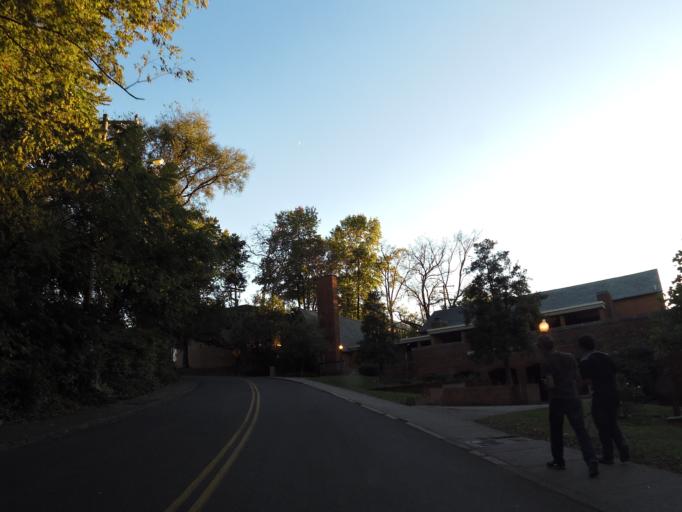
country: US
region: Tennessee
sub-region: Knox County
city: Knoxville
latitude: 35.9548
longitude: -83.9320
